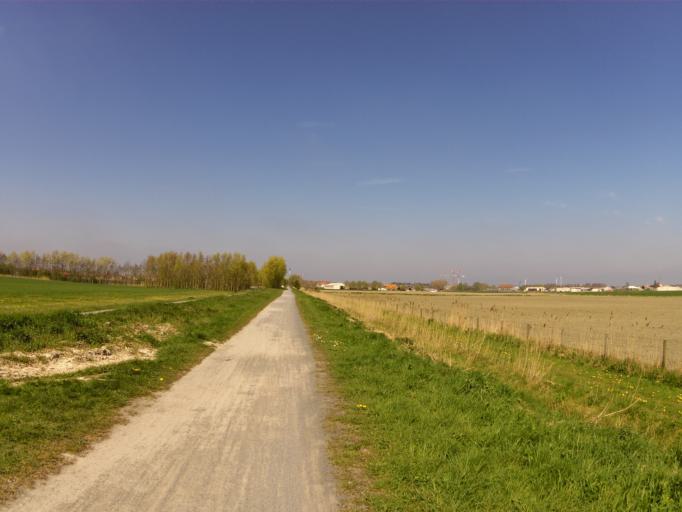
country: BE
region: Flanders
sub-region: Provincie West-Vlaanderen
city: Nieuwpoort
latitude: 51.1181
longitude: 2.7613
